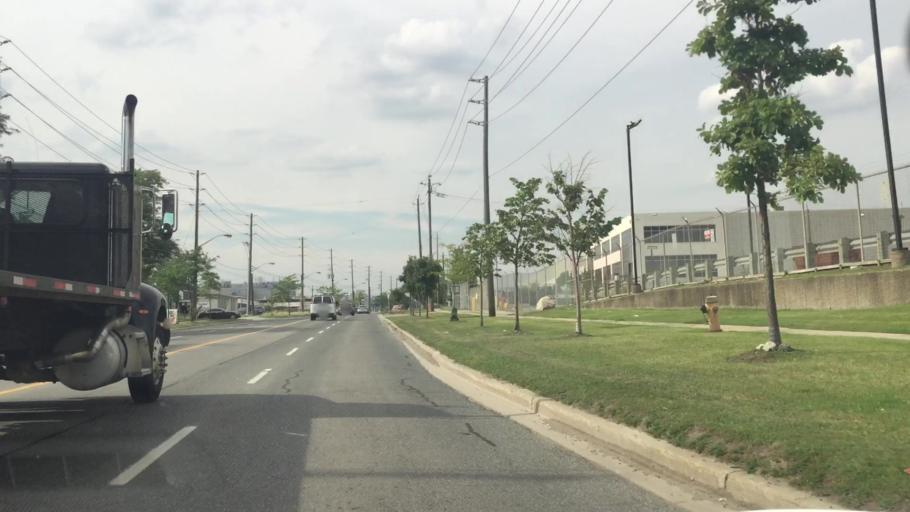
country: CA
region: Ontario
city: Concord
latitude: 43.7590
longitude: -79.5391
